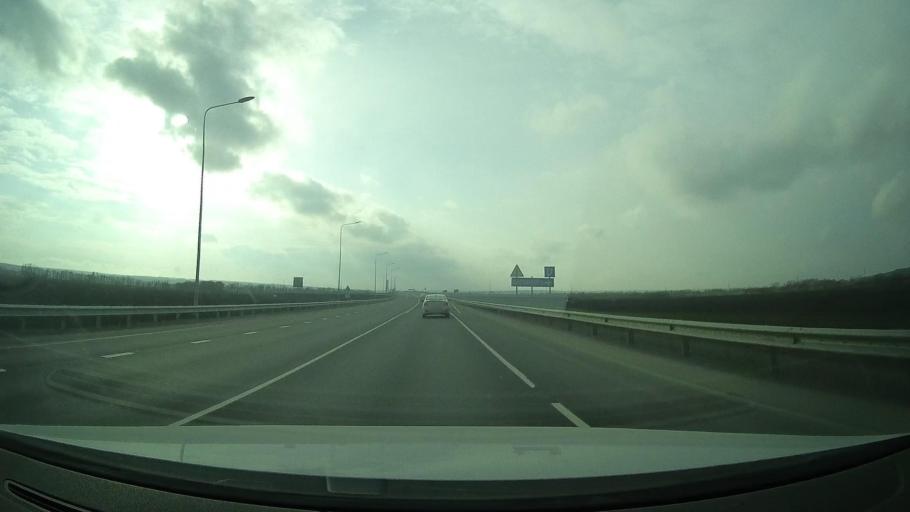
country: RU
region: Rostov
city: Grushevskaya
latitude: 47.4593
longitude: 39.8870
